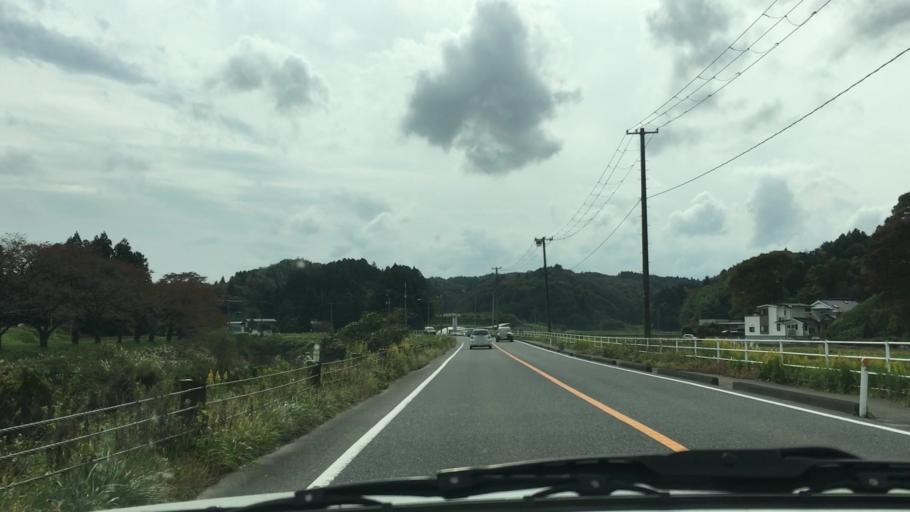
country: JP
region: Miyagi
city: Matsushima
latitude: 38.4319
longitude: 141.0615
